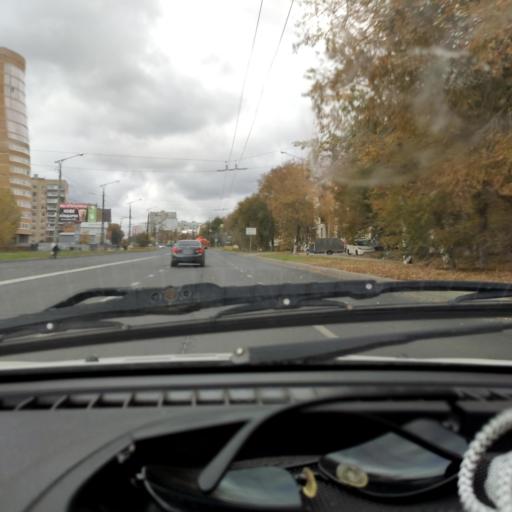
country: RU
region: Samara
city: Zhigulevsk
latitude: 53.4736
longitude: 49.4758
